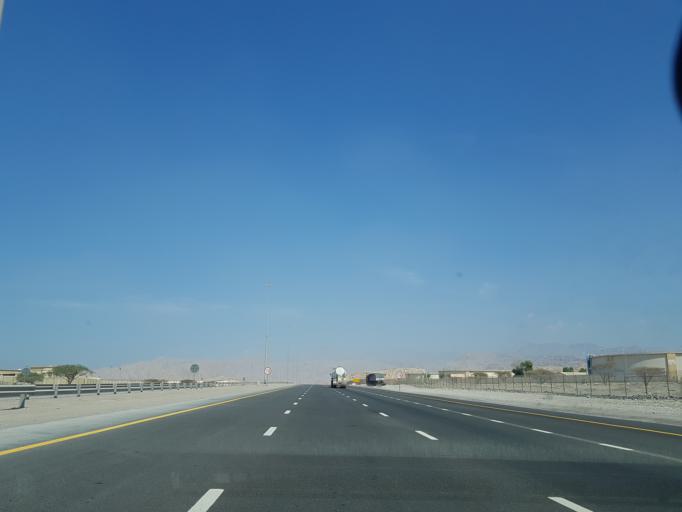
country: AE
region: Ra's al Khaymah
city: Ras al-Khaimah
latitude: 25.7699
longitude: 56.0267
